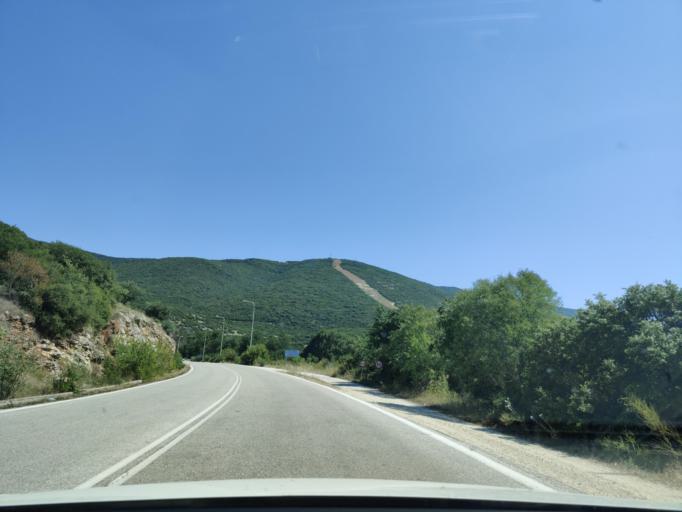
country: GR
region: East Macedonia and Thrace
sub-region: Nomos Kavalas
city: Zygos
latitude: 40.9982
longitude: 24.3808
